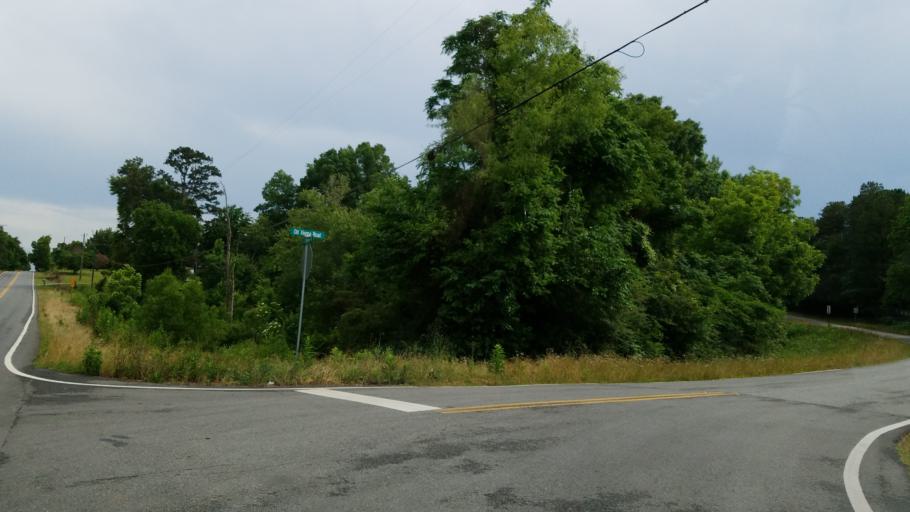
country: US
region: Georgia
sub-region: Dooly County
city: Unadilla
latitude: 32.3334
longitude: -83.7882
